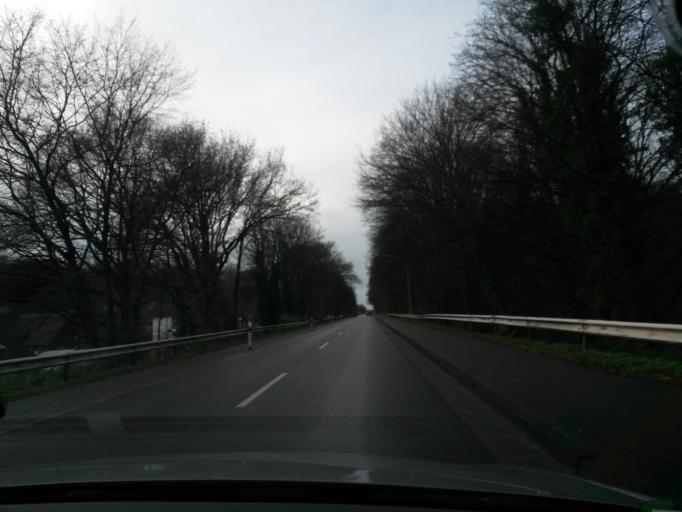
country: DE
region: North Rhine-Westphalia
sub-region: Regierungsbezirk Dusseldorf
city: Alpen
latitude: 51.5734
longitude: 6.5077
